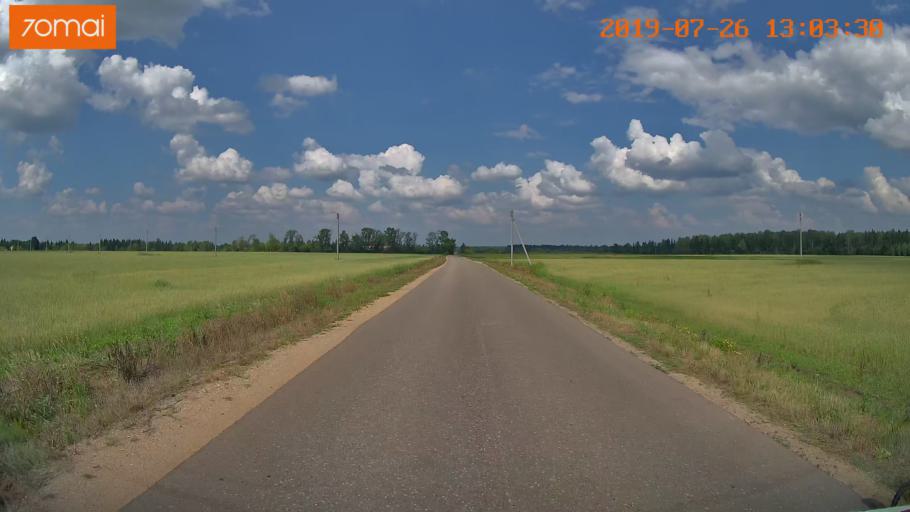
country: RU
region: Ivanovo
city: Bogorodskoye
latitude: 57.0463
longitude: 41.0222
